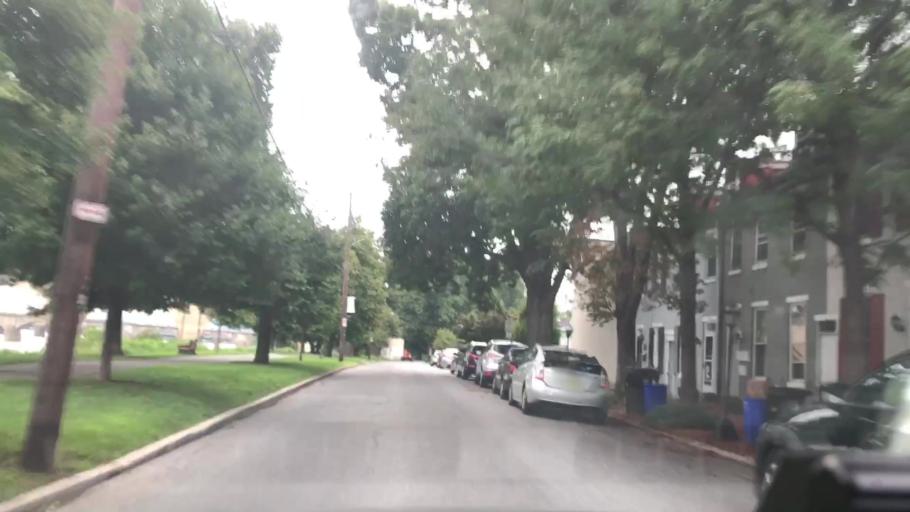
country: US
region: Pennsylvania
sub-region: Dauphin County
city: Harrisburg
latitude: 40.2539
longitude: -76.8763
